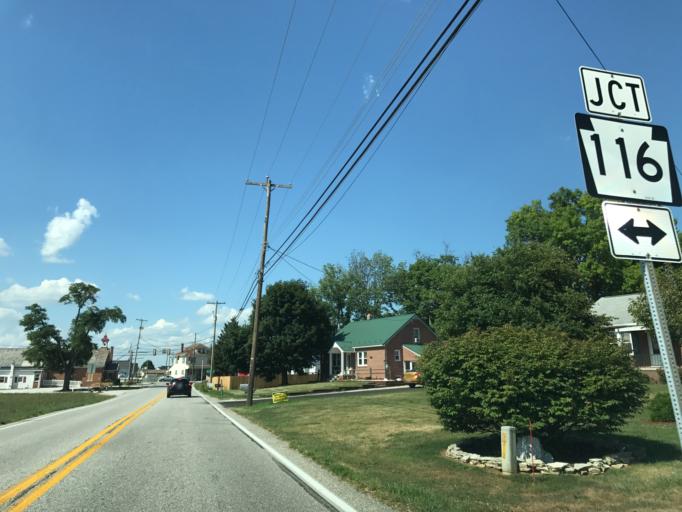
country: US
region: Pennsylvania
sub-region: Adams County
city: McSherrystown
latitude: 39.7954
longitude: -77.0404
